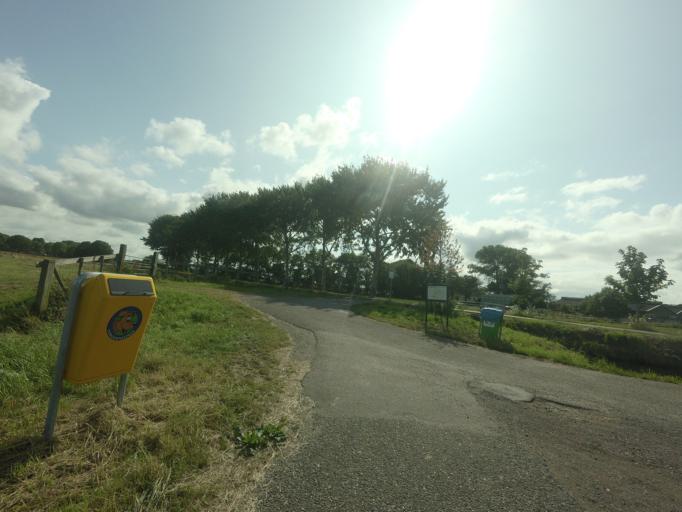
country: NL
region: North Holland
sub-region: Gemeente Haarlem
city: Haarlem
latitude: 52.4035
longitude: 4.6959
